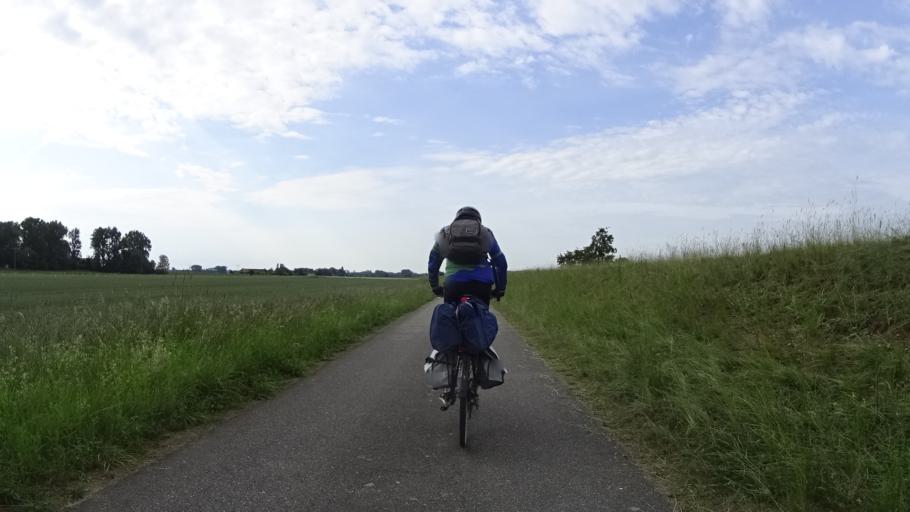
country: DE
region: Bavaria
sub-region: Lower Bavaria
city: Irlbach
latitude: 48.8607
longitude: 12.7634
